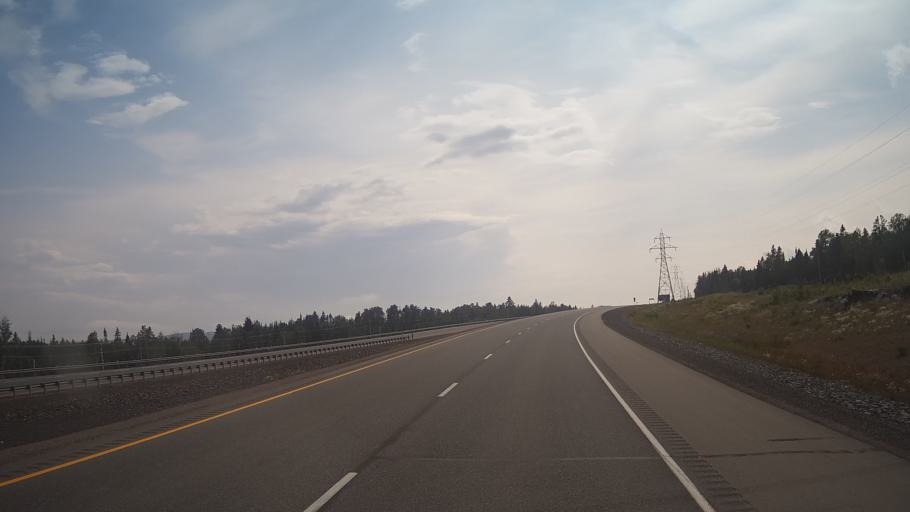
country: CA
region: Ontario
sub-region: Thunder Bay District
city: Thunder Bay
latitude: 48.5820
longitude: -88.8033
